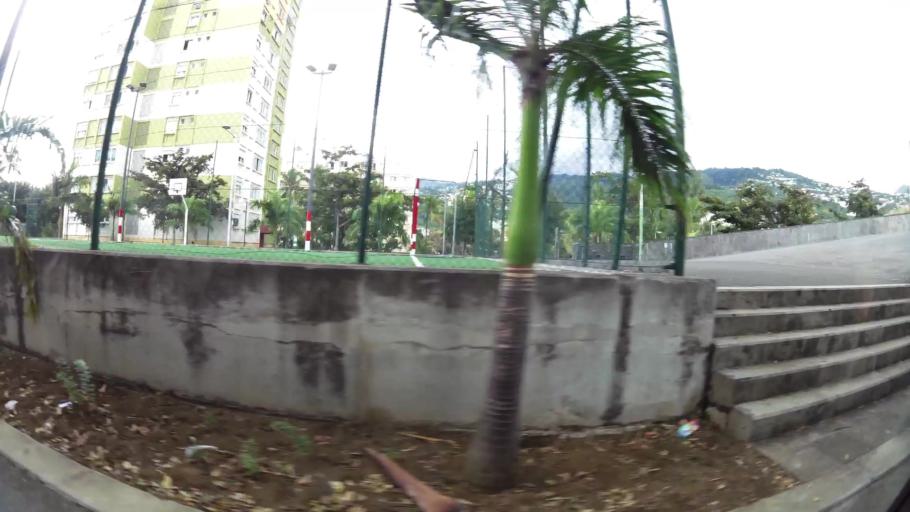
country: RE
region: Reunion
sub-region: Reunion
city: Saint-Denis
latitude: -20.8908
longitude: 55.4575
